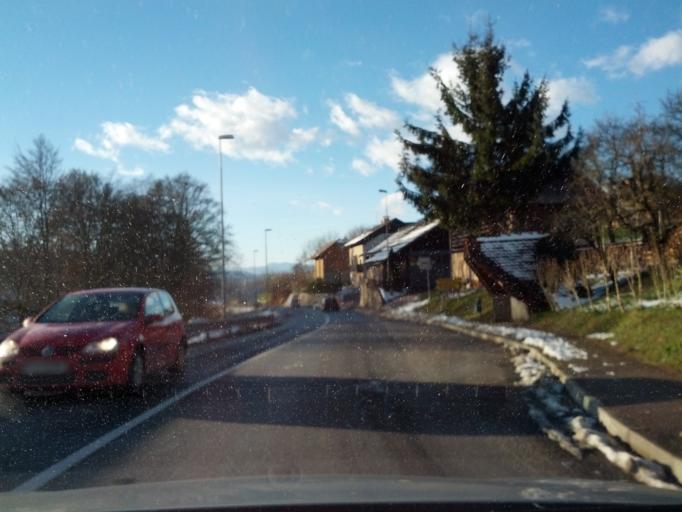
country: SI
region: Lukovica
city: Lukovica pri Domzalah
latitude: 46.1339
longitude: 14.6950
